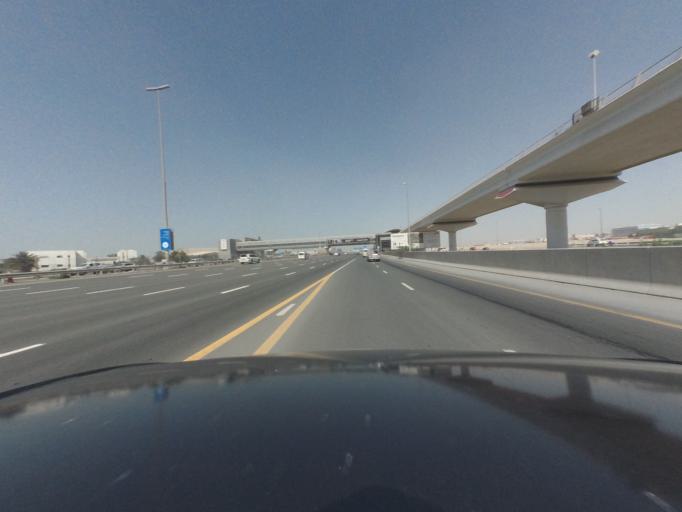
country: AE
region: Dubai
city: Dubai
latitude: 24.9994
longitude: 55.0952
